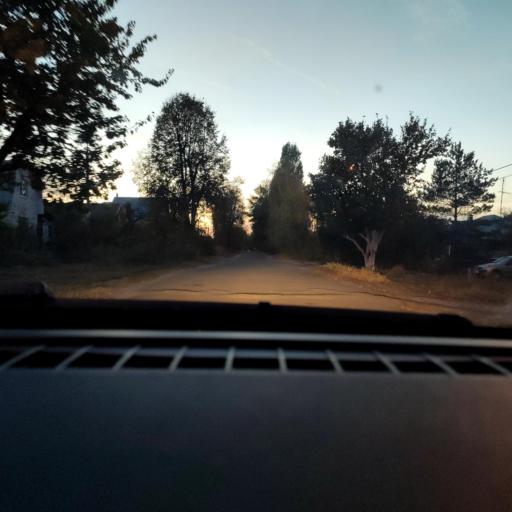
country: RU
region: Voronezj
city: Maslovka
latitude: 51.6152
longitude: 39.2700
